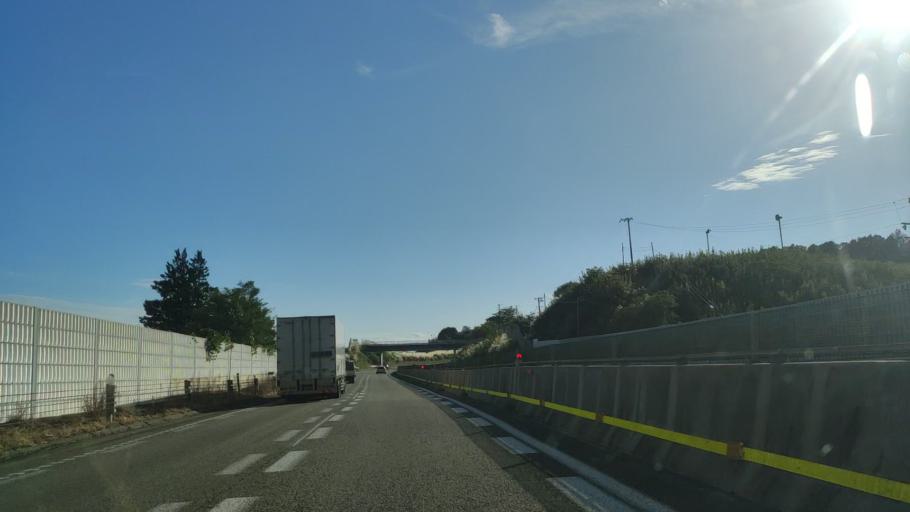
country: JP
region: Nagano
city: Iida
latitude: 35.5681
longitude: 137.8707
